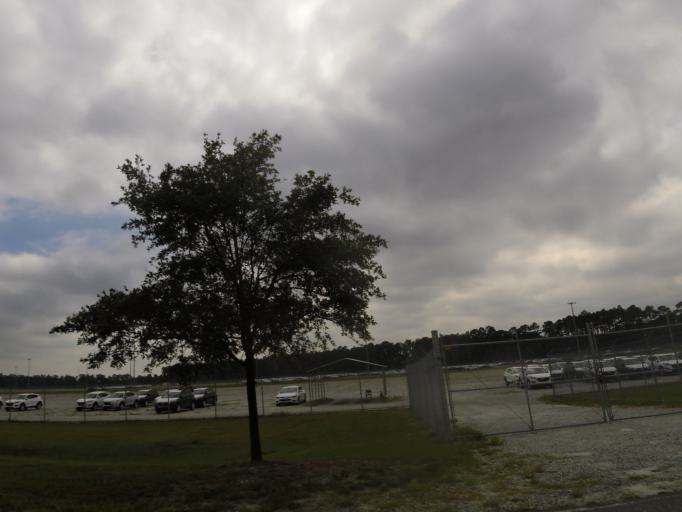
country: US
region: Georgia
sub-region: Glynn County
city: Brunswick
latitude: 31.1122
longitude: -81.5432
